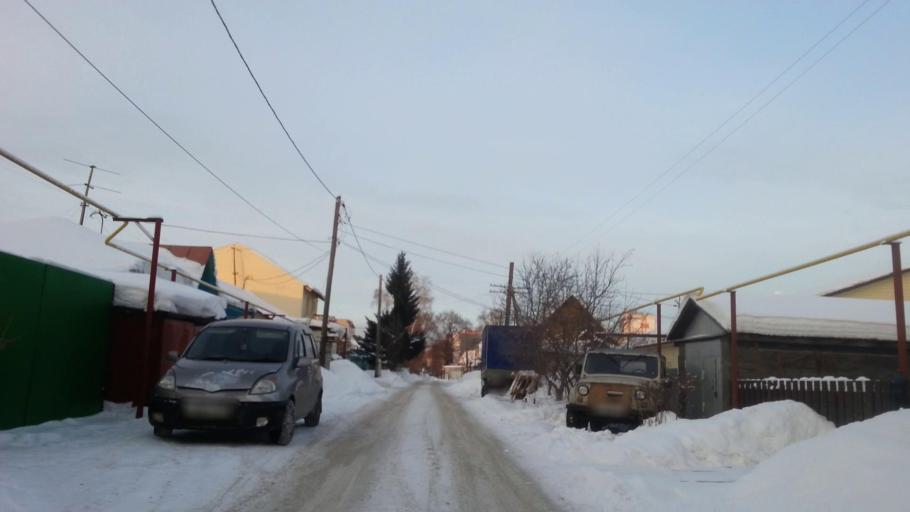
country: RU
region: Altai Krai
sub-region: Gorod Barnaulskiy
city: Barnaul
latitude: 53.3524
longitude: 83.6919
